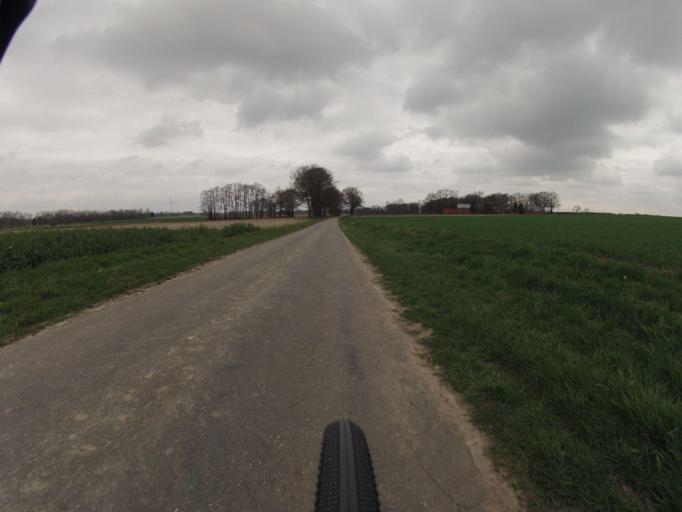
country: DE
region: North Rhine-Westphalia
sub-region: Regierungsbezirk Munster
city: Mettingen
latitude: 52.3322
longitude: 7.8204
